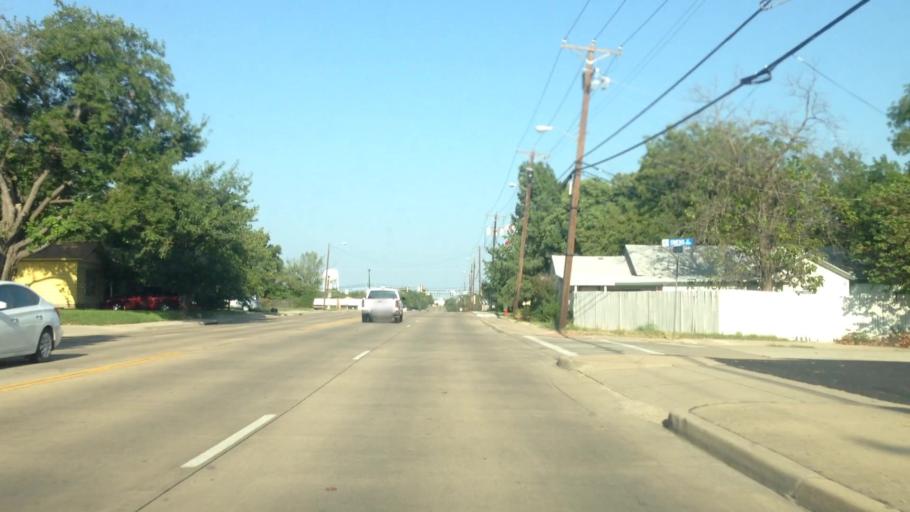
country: US
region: Texas
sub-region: Tarrant County
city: Haltom City
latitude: 32.8096
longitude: -97.2759
